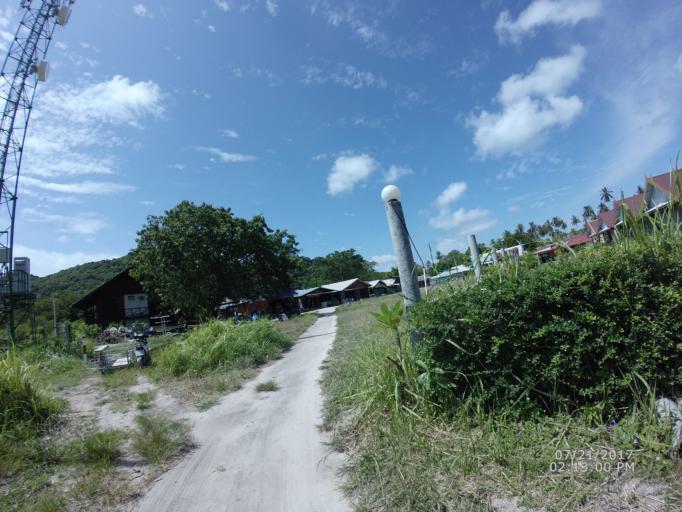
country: TH
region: Phangnga
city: Ban Phru Nai
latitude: 7.7612
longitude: 98.7697
